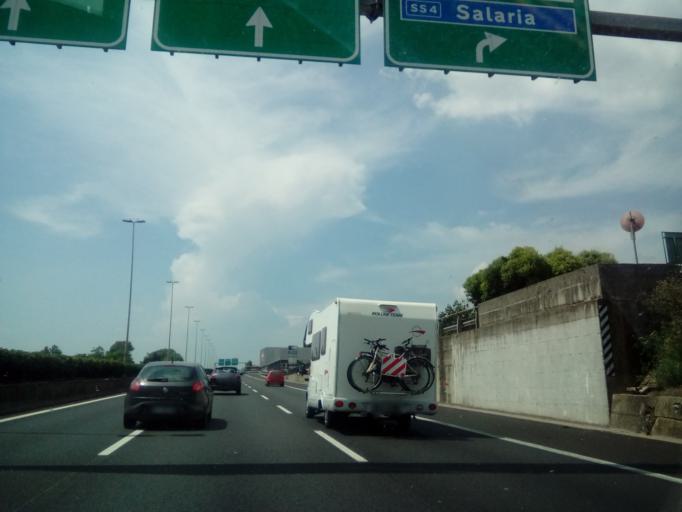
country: IT
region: Latium
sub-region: Citta metropolitana di Roma Capitale
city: Colle Verde
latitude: 41.9701
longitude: 12.5551
